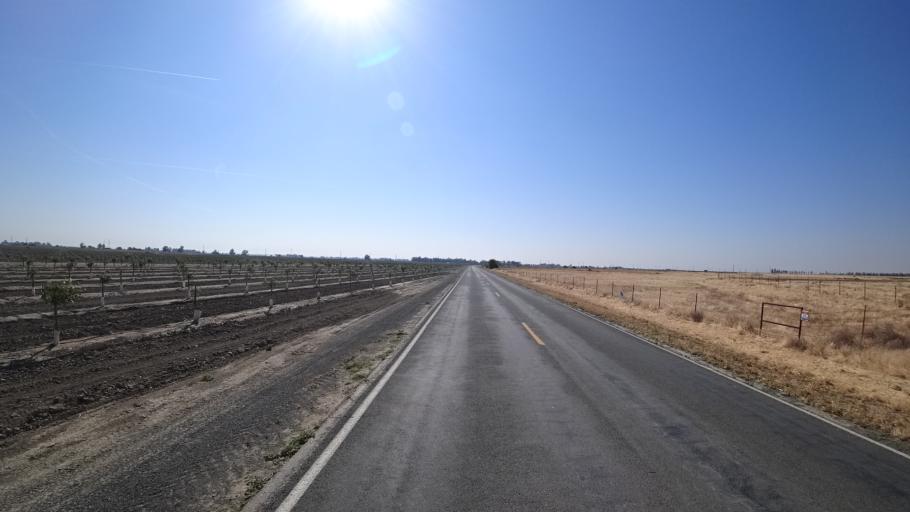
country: US
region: California
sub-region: Fresno County
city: Riverdale
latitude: 36.3604
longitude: -119.9110
